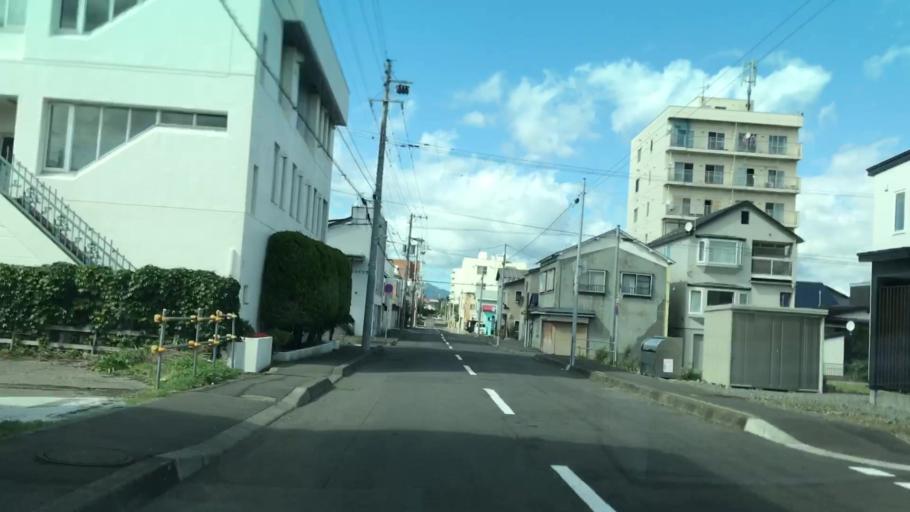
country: JP
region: Hokkaido
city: Muroran
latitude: 42.3123
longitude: 140.9715
